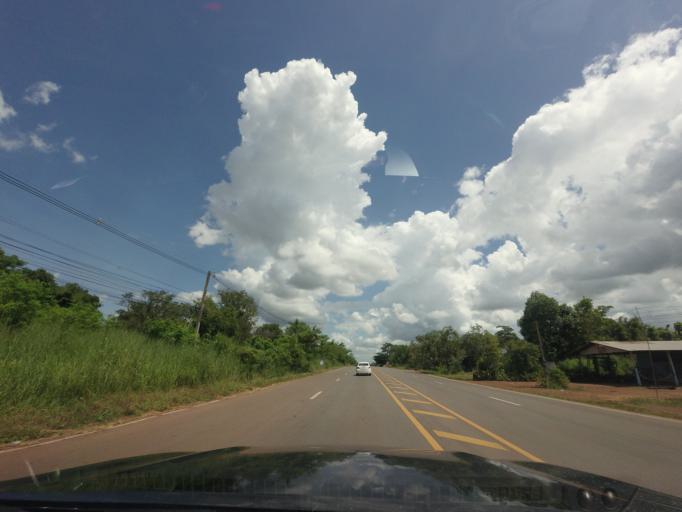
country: TH
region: Changwat Udon Thani
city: Ban Dung
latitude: 17.6844
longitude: 103.2110
